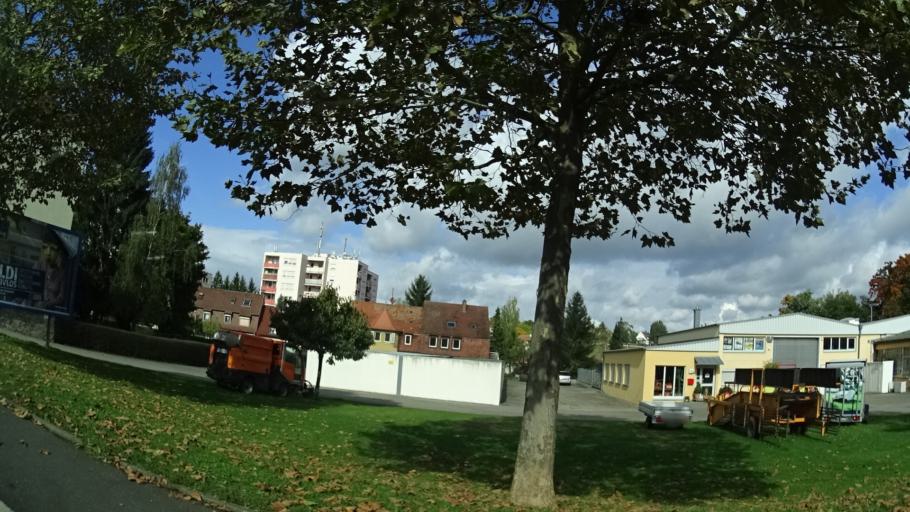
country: DE
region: Bavaria
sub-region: Regierungsbezirk Unterfranken
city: Kitzingen
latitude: 49.7365
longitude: 10.1531
